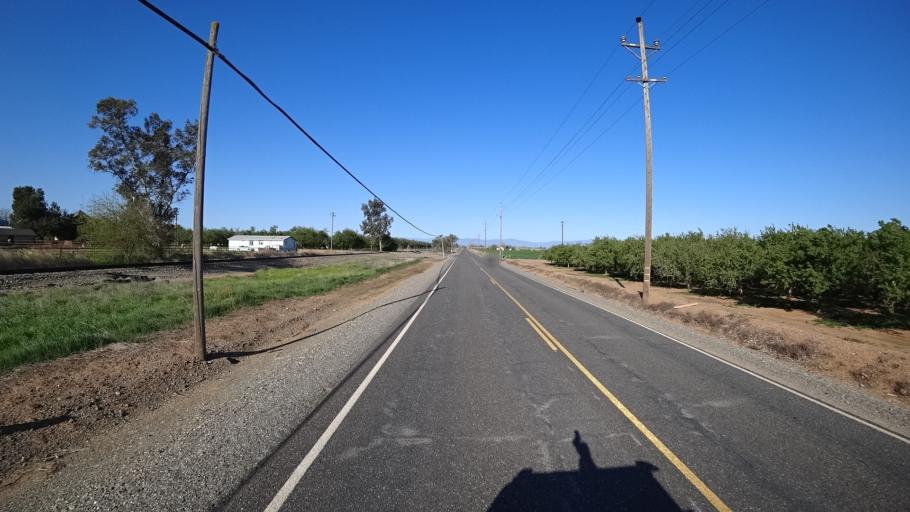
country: US
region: California
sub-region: Glenn County
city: Orland
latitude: 39.7685
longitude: -122.1310
